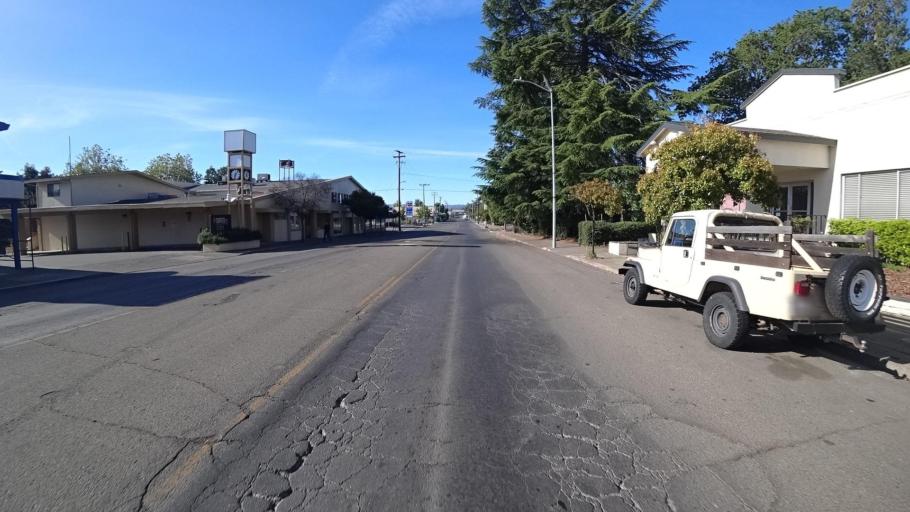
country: US
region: California
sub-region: Lake County
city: Lakeport
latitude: 39.0420
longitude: -122.9152
